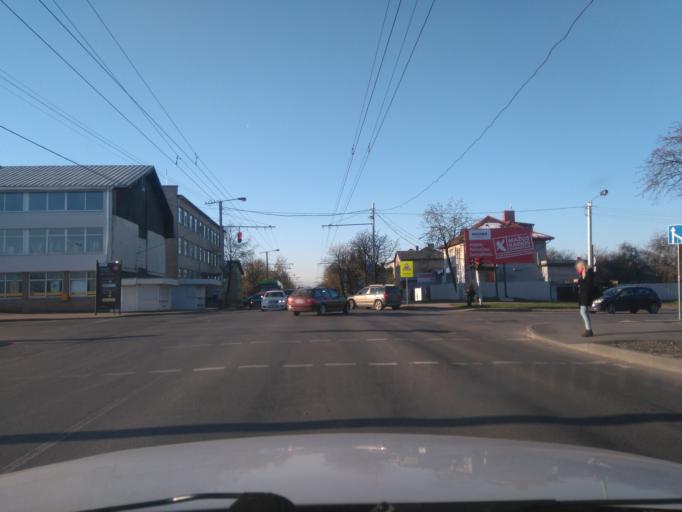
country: LT
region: Kauno apskritis
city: Dainava (Kaunas)
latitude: 54.9056
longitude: 23.9738
